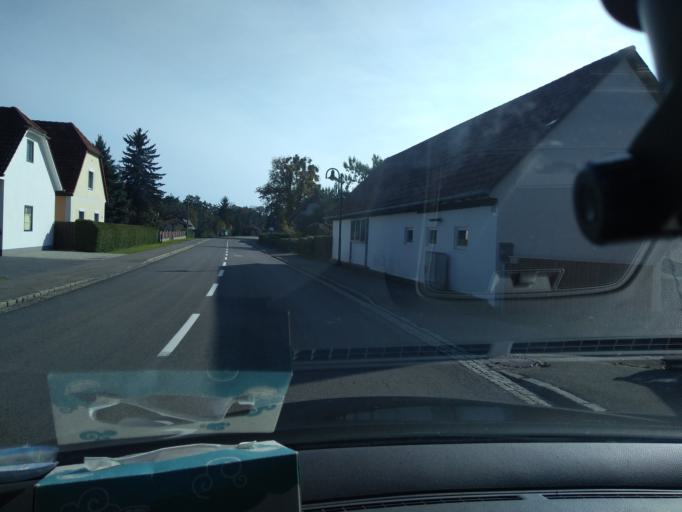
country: AT
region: Styria
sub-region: Politischer Bezirk Leibnitz
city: Stocking
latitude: 46.8509
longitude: 15.5368
